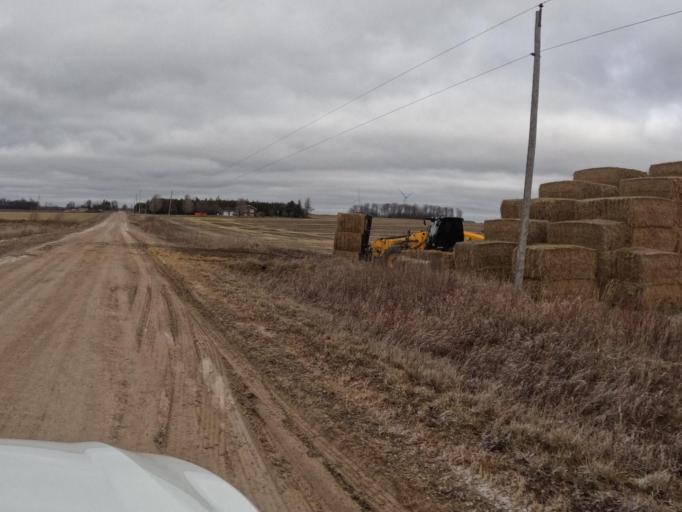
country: CA
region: Ontario
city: Shelburne
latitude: 44.0189
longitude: -80.3686
